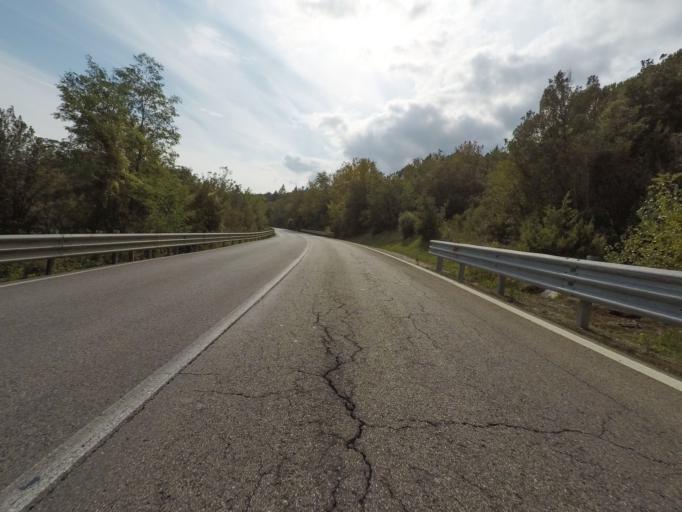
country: IT
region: Tuscany
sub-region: Provincia di Siena
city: Murlo
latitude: 43.1343
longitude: 11.2906
